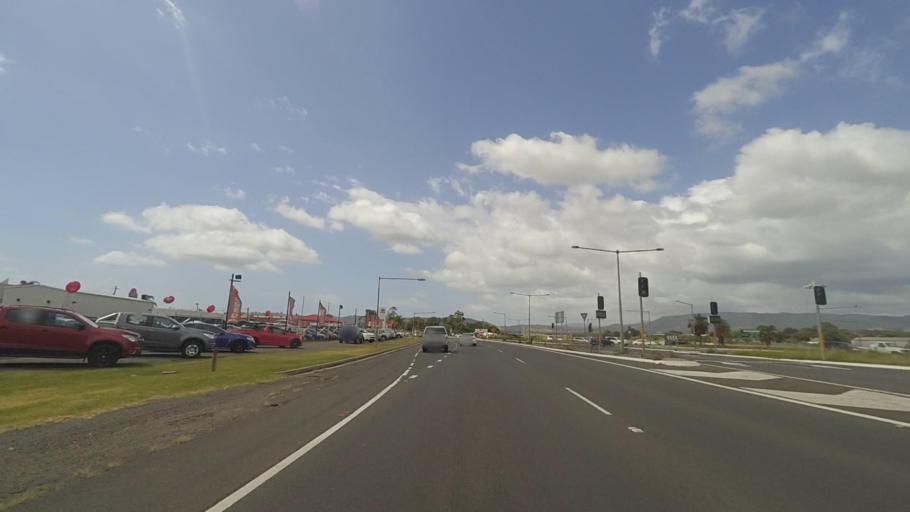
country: AU
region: New South Wales
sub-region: Shellharbour
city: Albion Park Rail
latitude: -34.5486
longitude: 150.7855
